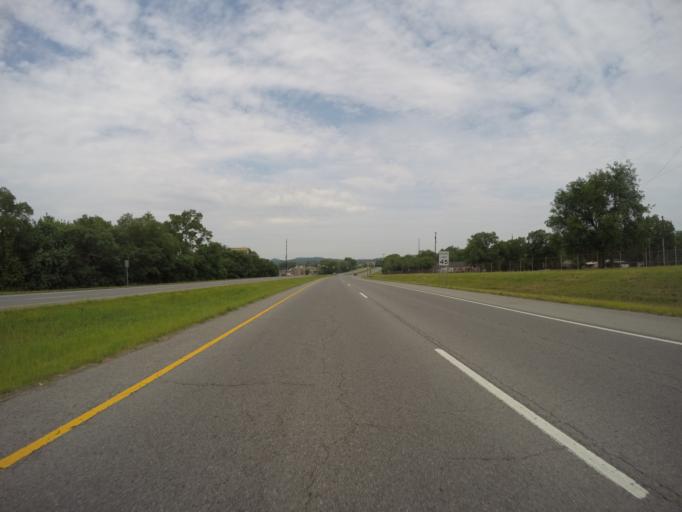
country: US
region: Tennessee
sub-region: Davidson County
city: Goodlettsville
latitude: 36.2639
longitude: -86.7022
